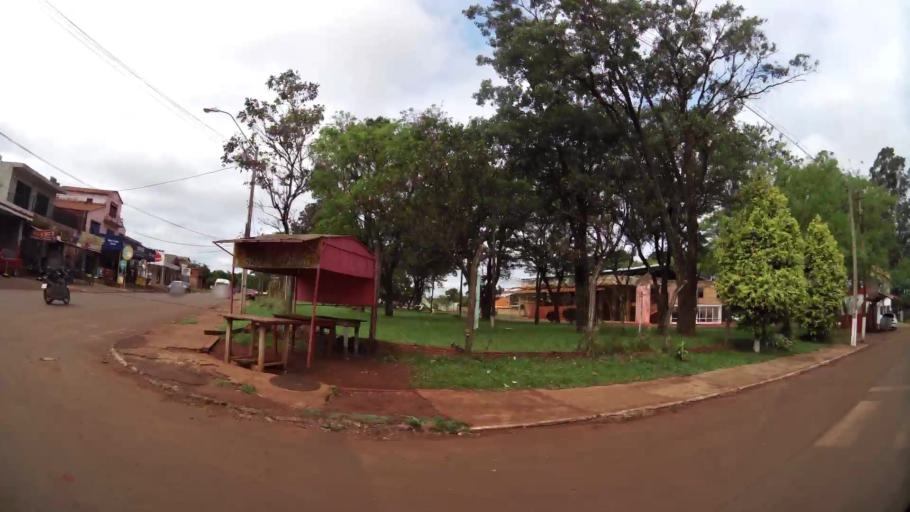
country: PY
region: Alto Parana
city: Ciudad del Este
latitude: -25.3890
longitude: -54.6462
